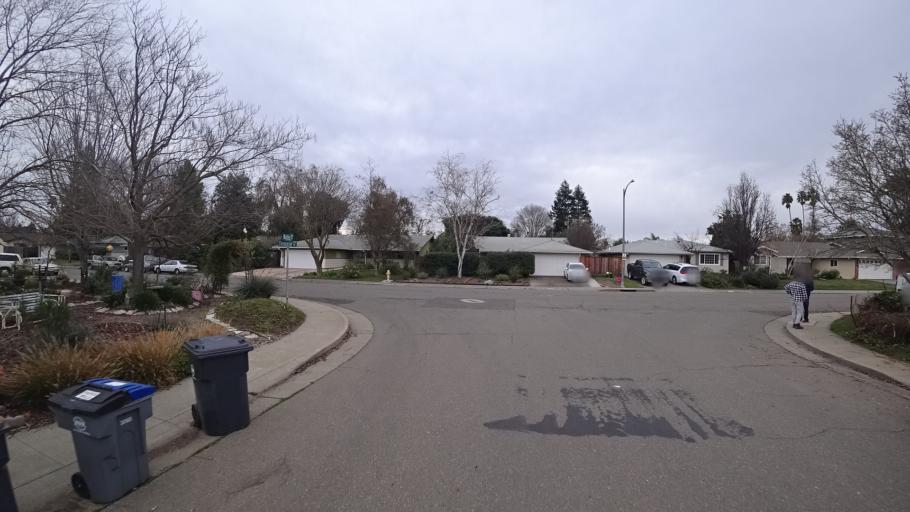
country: US
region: California
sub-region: Yolo County
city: Davis
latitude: 38.5616
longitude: -121.7231
